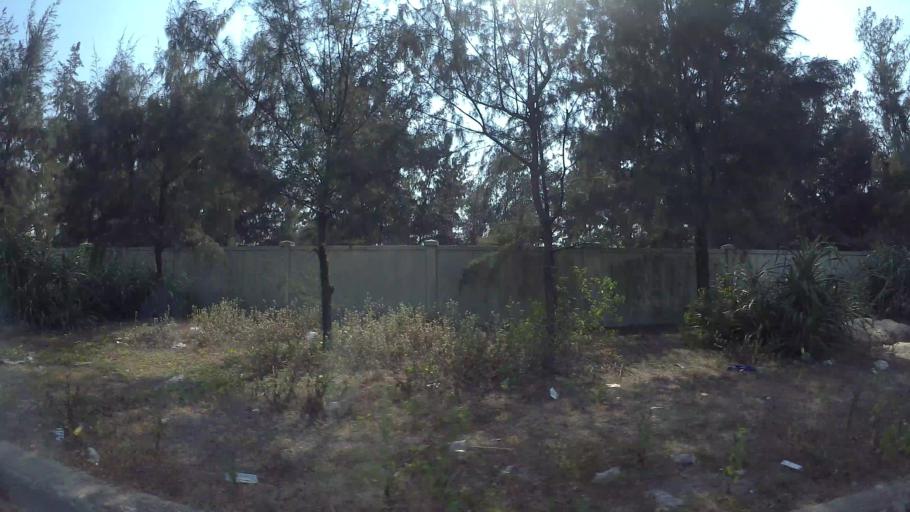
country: VN
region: Da Nang
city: Ngu Hanh Son
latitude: 15.9700
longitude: 108.2827
